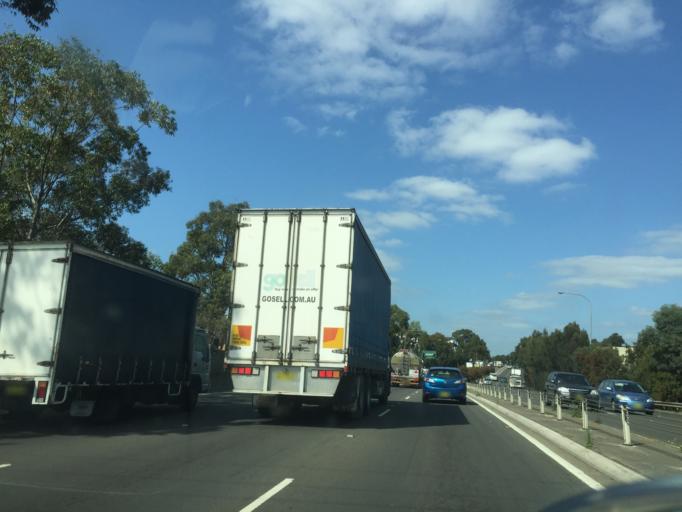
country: AU
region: New South Wales
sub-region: Strathfield
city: Homebush
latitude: -33.8644
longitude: 151.0662
